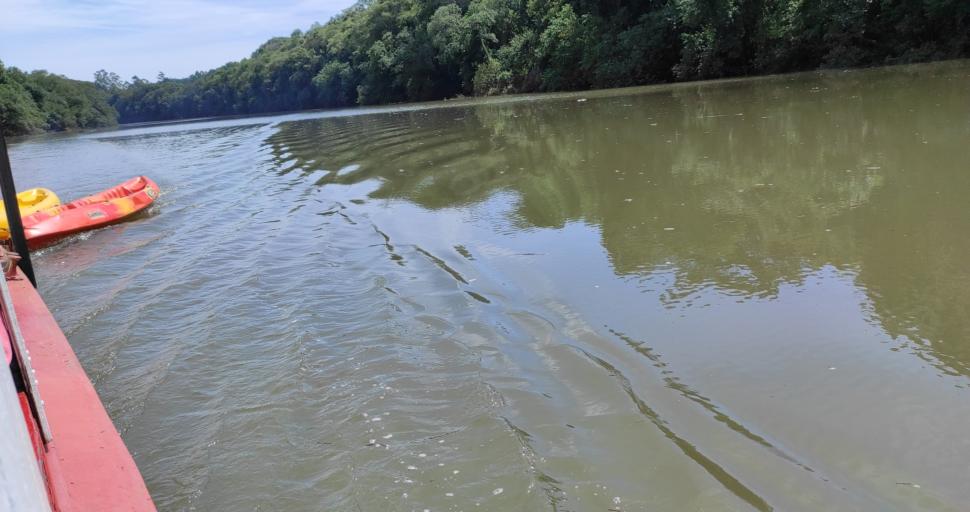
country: AR
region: Misiones
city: El Soberbio
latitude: -27.2879
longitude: -54.1947
